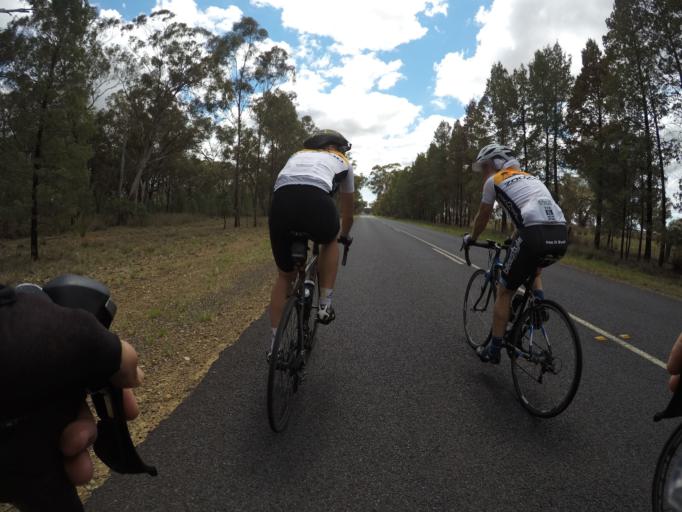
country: AU
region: New South Wales
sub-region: Dubbo Municipality
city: Dubbo
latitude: -32.4832
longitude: 148.5584
